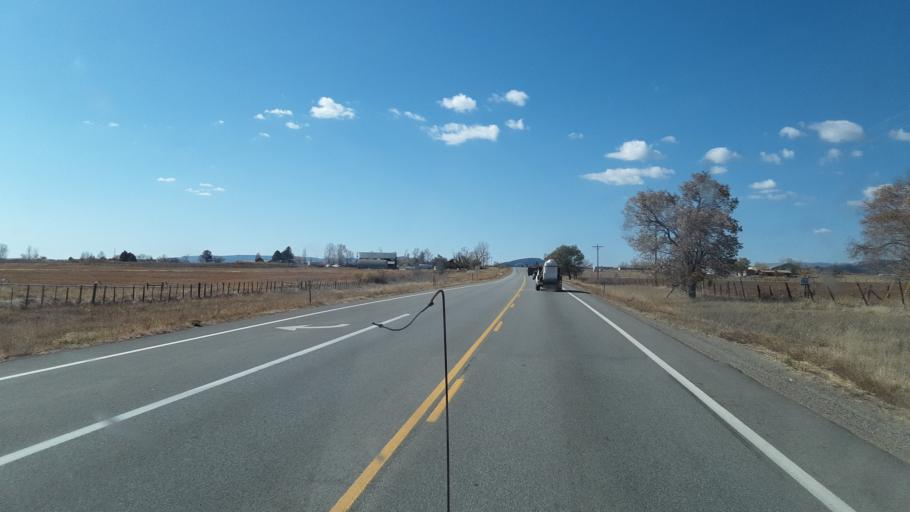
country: US
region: Colorado
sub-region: La Plata County
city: Durango
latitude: 37.2298
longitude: -107.7680
